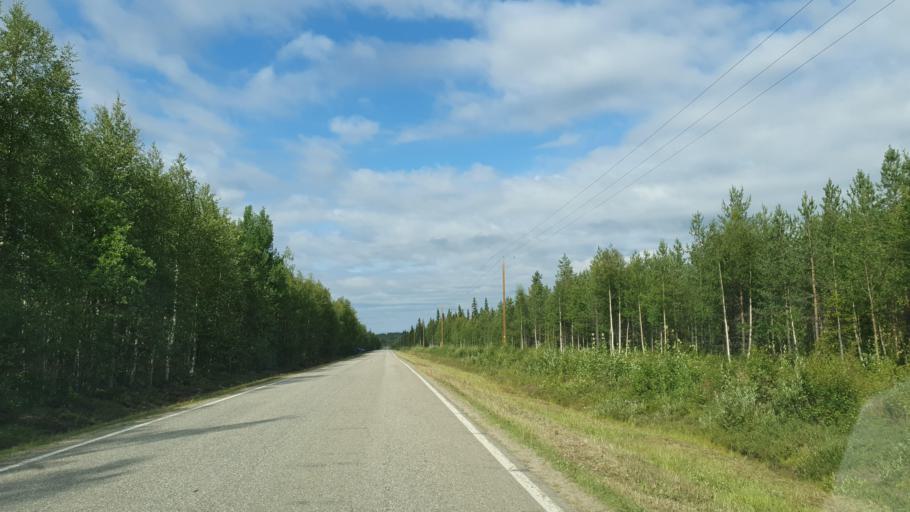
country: FI
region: Lapland
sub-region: Pohjois-Lappi
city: Sodankylae
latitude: 67.5412
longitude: 25.9333
